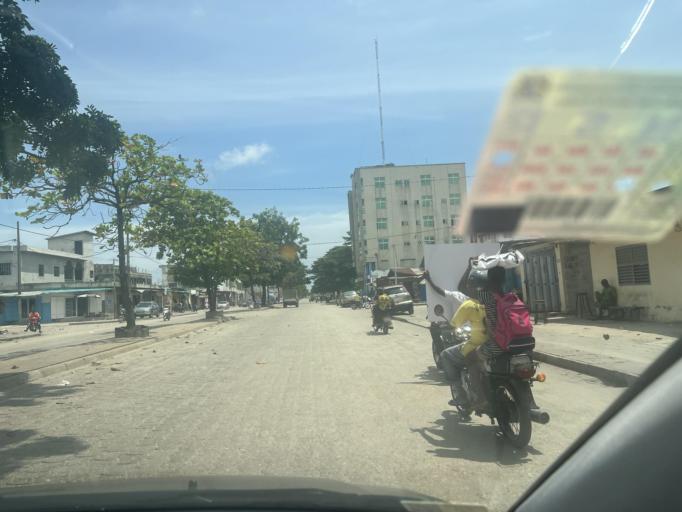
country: BJ
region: Littoral
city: Cotonou
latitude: 6.3821
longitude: 2.4470
